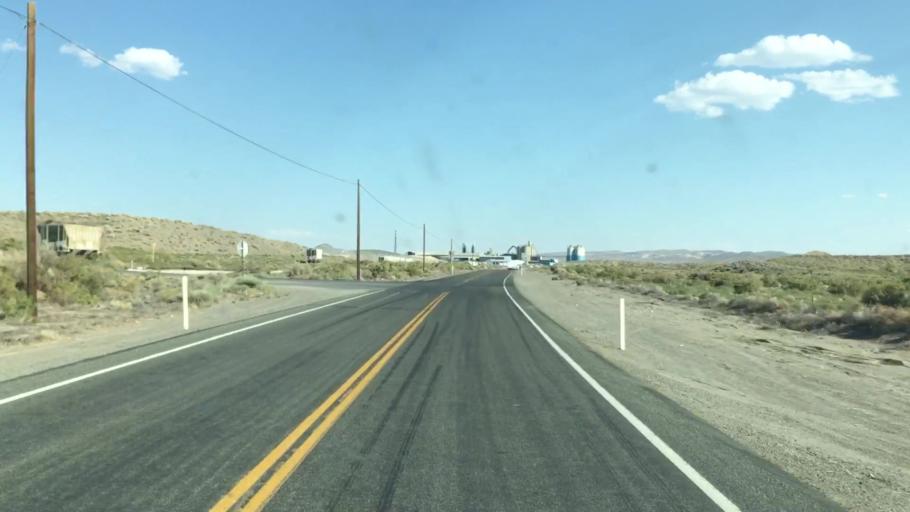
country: US
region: Nevada
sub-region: Lyon County
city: Fernley
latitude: 39.6292
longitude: -119.2758
